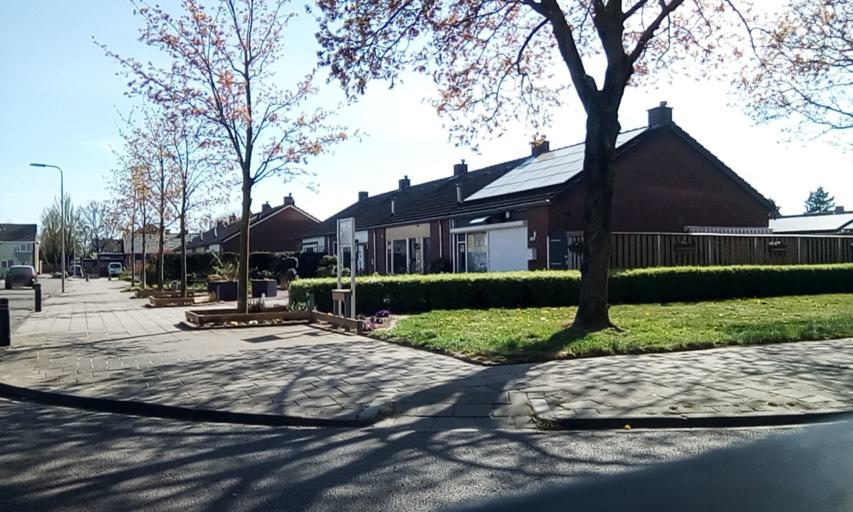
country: NL
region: Gelderland
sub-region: Gemeente Wijchen
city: Wijchen
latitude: 51.8117
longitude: 5.7122
